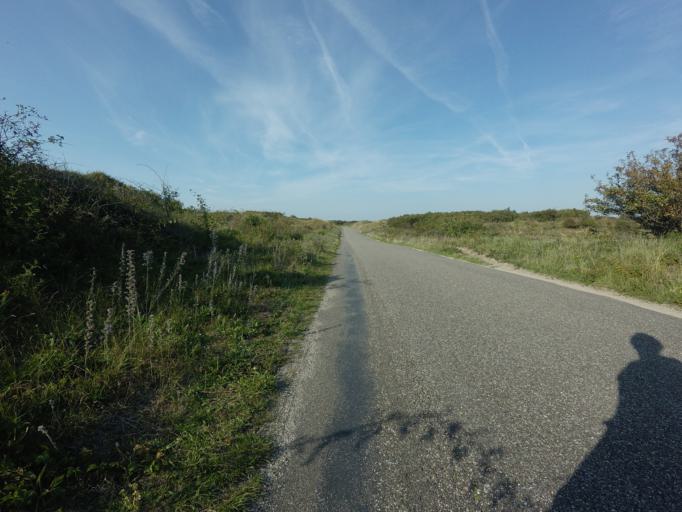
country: NL
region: Friesland
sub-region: Gemeente Schiermonnikoog
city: Schiermonnikoog
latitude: 53.4900
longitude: 6.1829
